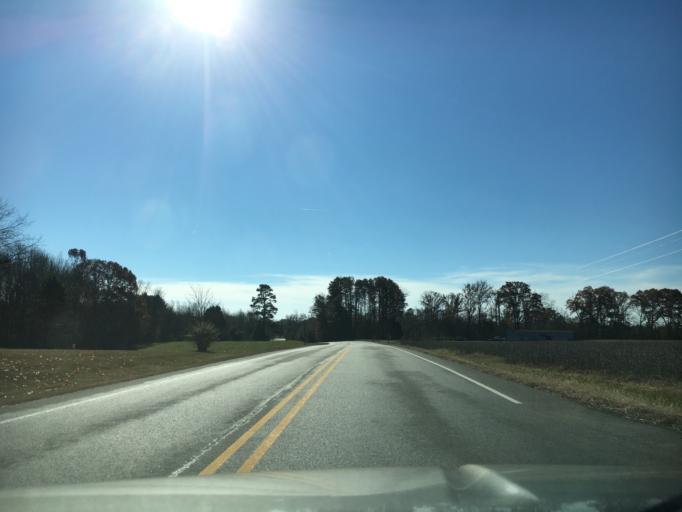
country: US
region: Virginia
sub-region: Cumberland County
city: Cumberland
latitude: 37.5605
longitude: -78.1852
